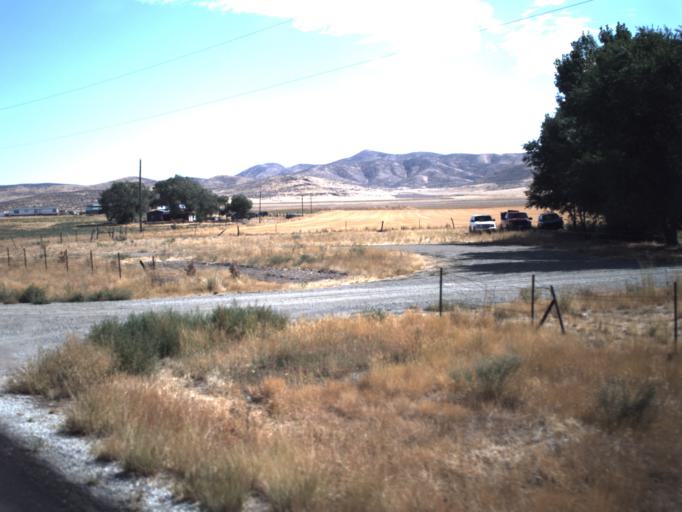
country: US
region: Utah
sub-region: Box Elder County
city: Garland
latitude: 41.7842
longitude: -112.4335
